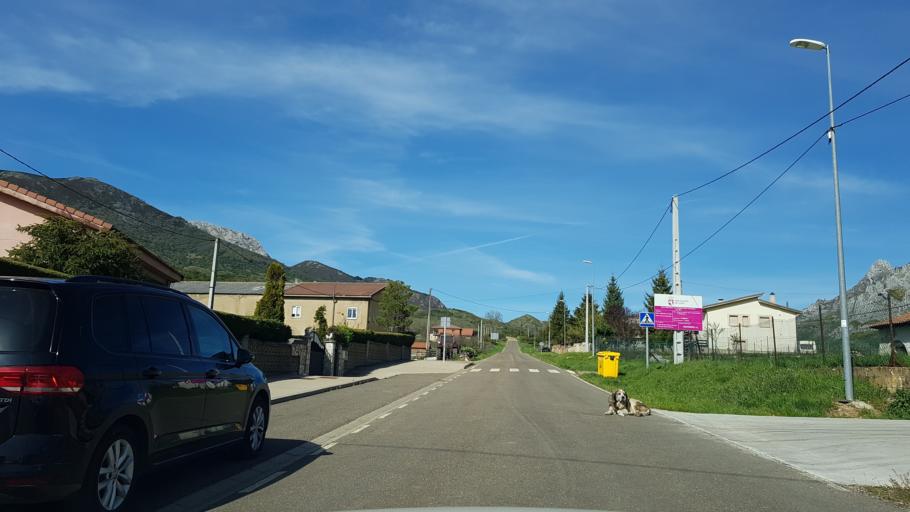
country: ES
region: Castille and Leon
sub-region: Provincia de Leon
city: Carmenes
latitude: 42.9585
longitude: -5.5788
